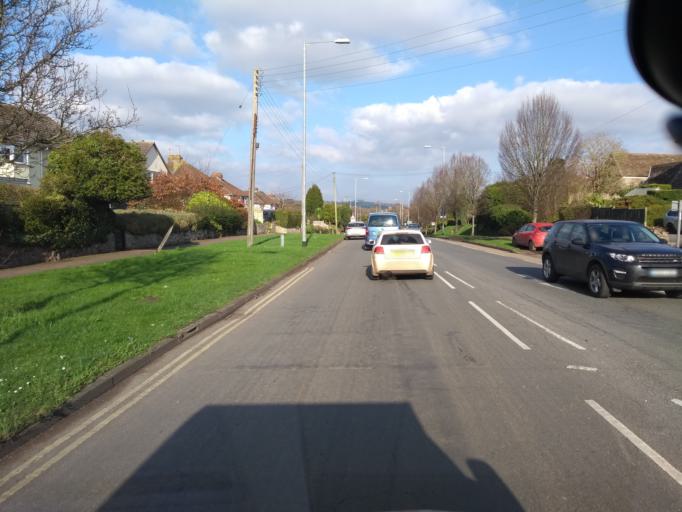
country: GB
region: England
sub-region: Somerset
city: Taunton
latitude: 51.0184
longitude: -3.0736
